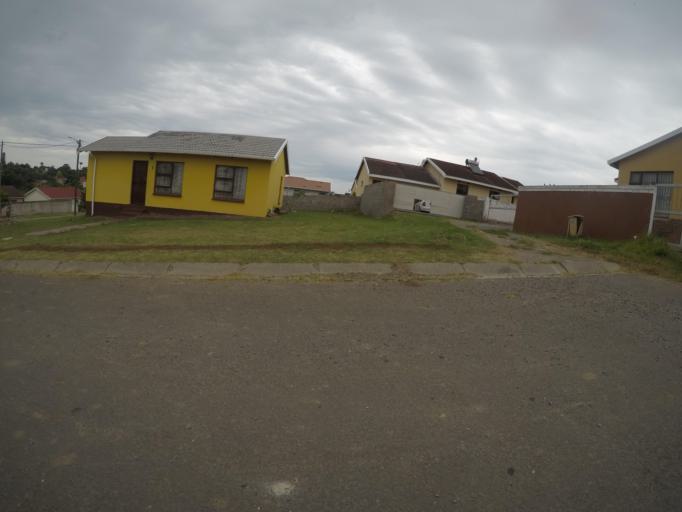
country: ZA
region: Eastern Cape
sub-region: Buffalo City Metropolitan Municipality
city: East London
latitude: -32.9939
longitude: 27.8464
